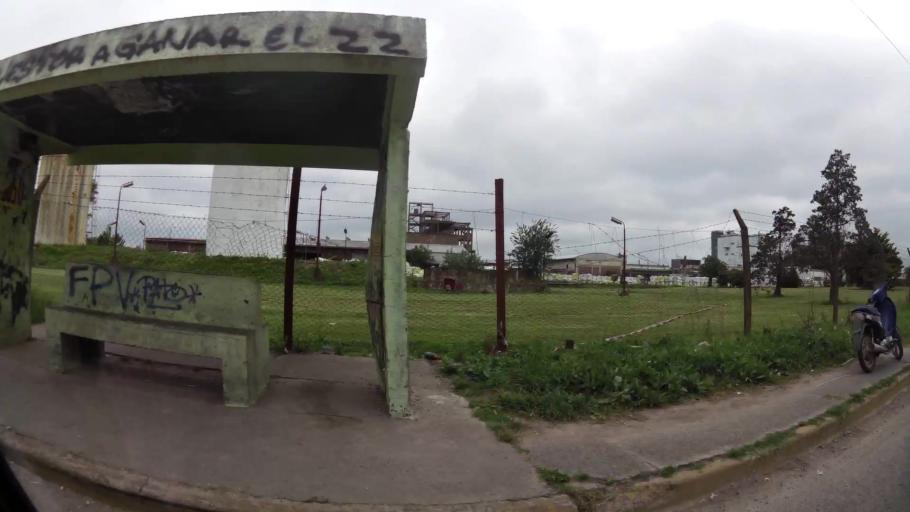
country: AR
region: Buenos Aires
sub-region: Partido de La Plata
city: La Plata
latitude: -34.9815
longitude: -58.0329
